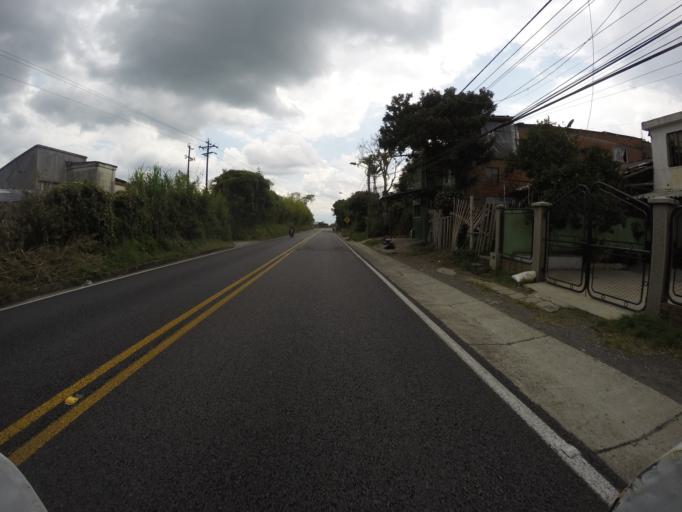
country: CO
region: Risaralda
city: Pereira
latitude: 4.7650
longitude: -75.6876
